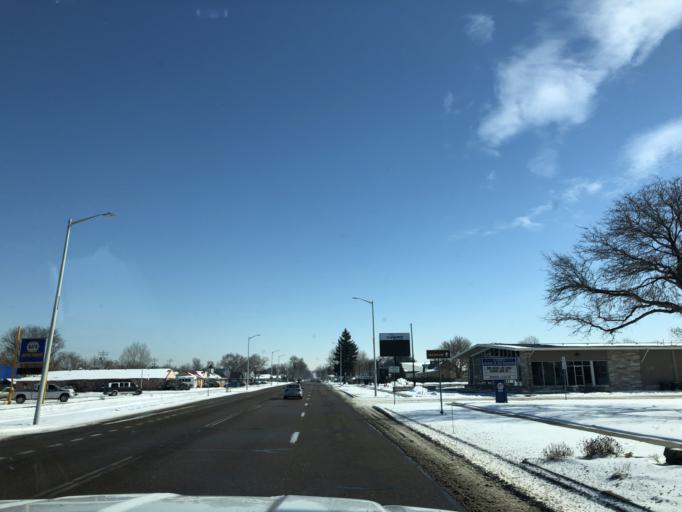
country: US
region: Colorado
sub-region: Morgan County
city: Fort Morgan
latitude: 40.2540
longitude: -103.8154
